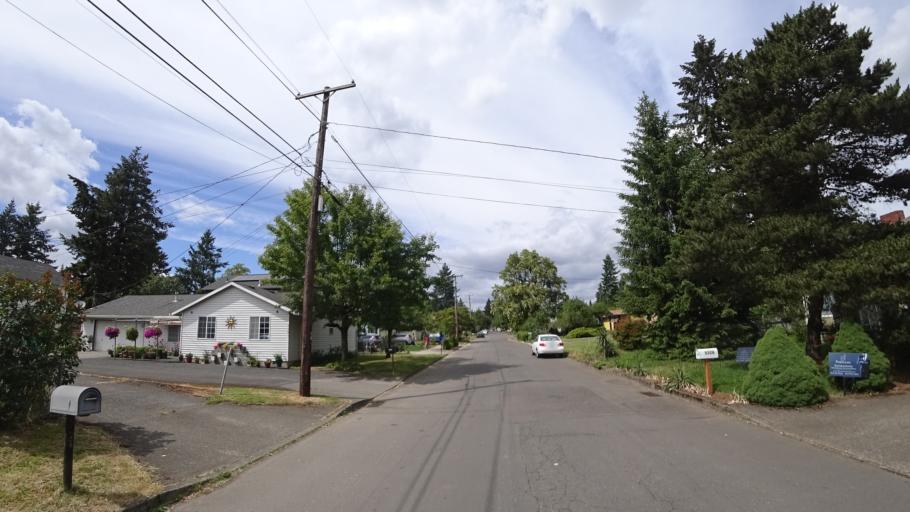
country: US
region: Oregon
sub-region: Multnomah County
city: Lents
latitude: 45.4839
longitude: -122.5513
